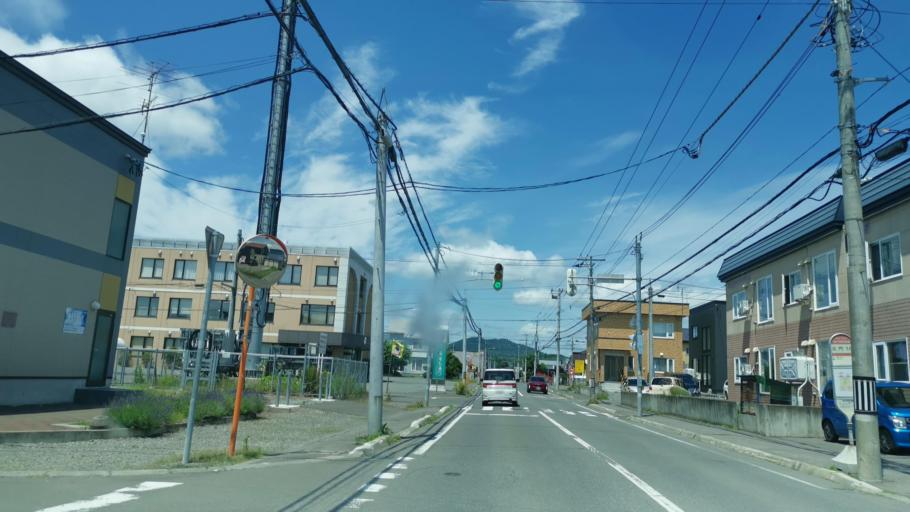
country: JP
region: Hokkaido
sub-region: Asahikawa-shi
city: Asahikawa
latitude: 43.7908
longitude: 142.3375
